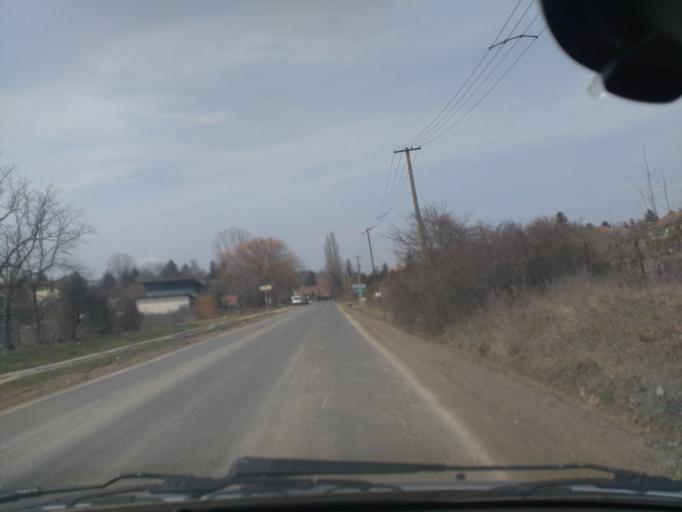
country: HU
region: Pest
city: Pilisborosjeno
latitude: 47.6038
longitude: 18.9981
